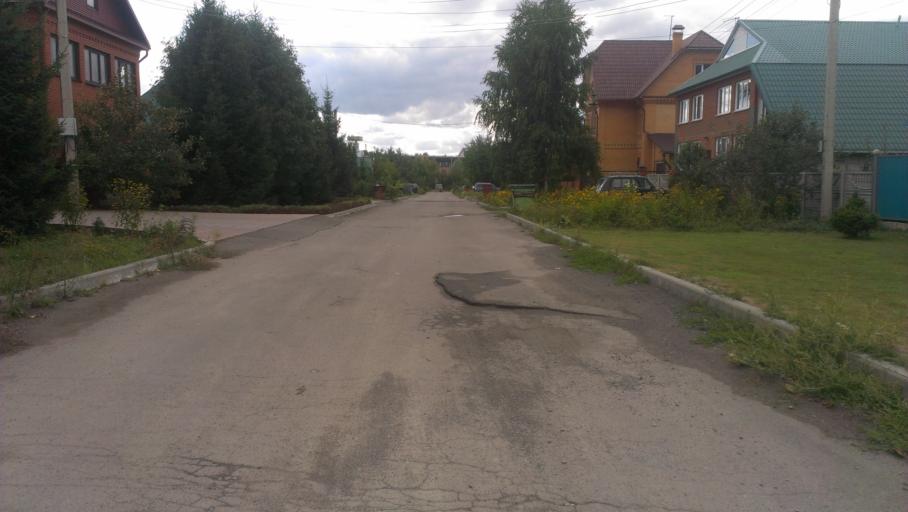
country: RU
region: Altai Krai
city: Novosilikatnyy
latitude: 53.3511
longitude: 83.6474
